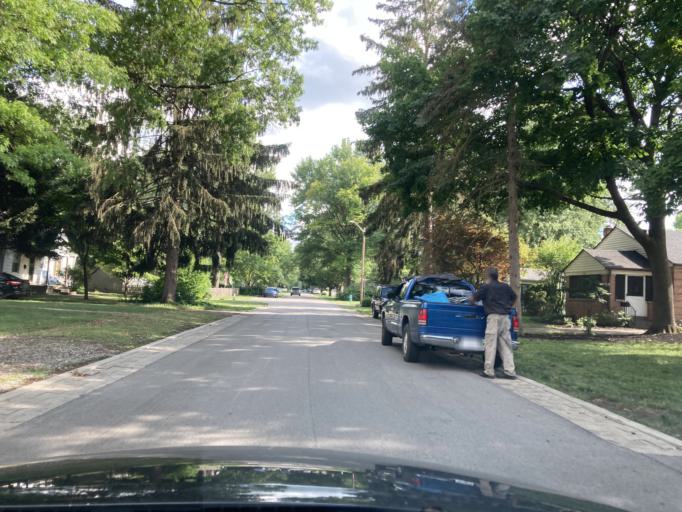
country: US
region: Indiana
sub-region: Marion County
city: Broad Ripple
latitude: 39.8593
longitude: -86.1340
